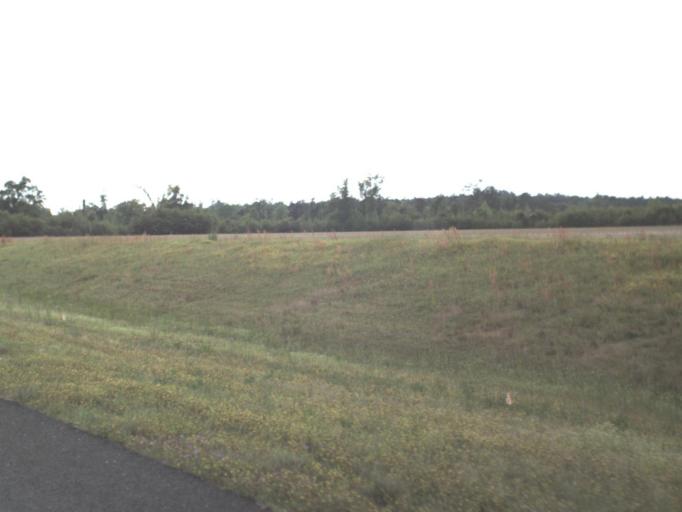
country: US
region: Florida
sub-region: Escambia County
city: Century
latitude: 30.9420
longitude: -87.2905
